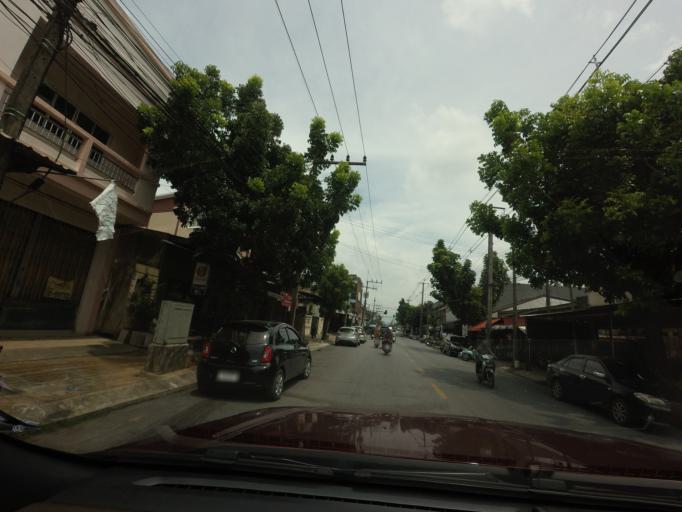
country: TH
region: Yala
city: Yala
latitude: 6.5506
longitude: 101.2949
